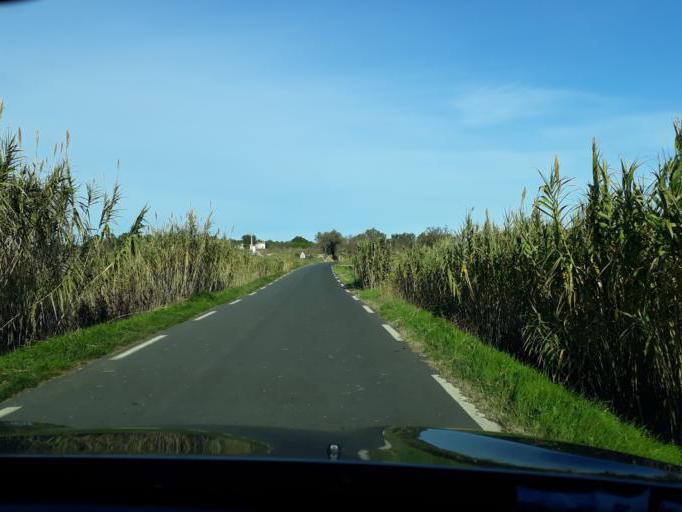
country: FR
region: Languedoc-Roussillon
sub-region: Departement de l'Herault
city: Castelnau-de-Guers
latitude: 43.4247
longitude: 3.4320
